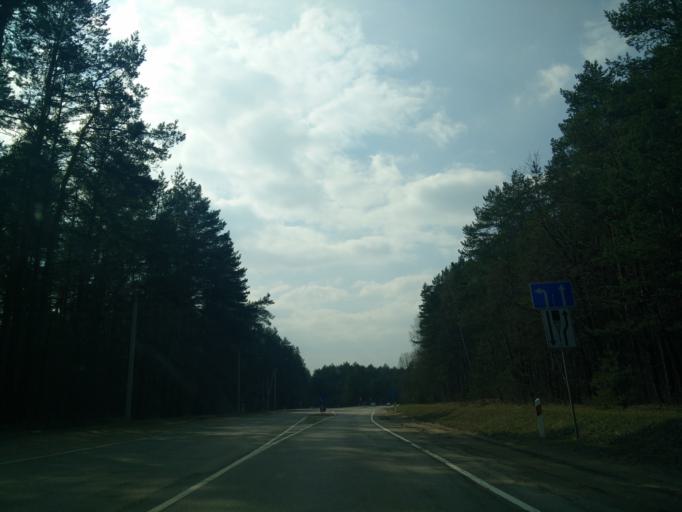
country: LT
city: Baltoji Voke
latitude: 54.6366
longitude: 25.1741
